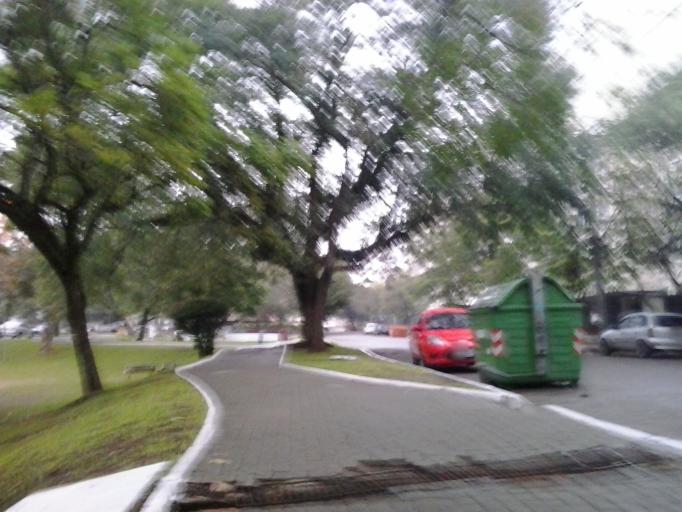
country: BR
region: Rio Grande do Sul
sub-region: Santa Maria
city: Santa Maria
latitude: -29.6885
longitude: -53.8019
